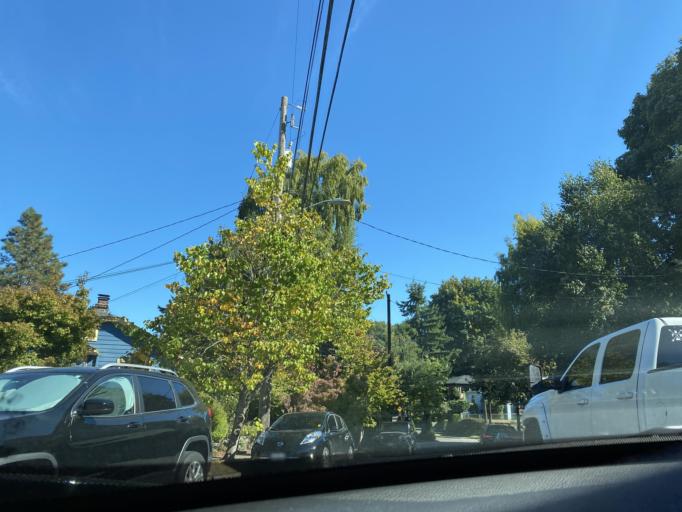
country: US
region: Washington
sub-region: King County
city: Seattle
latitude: 47.6447
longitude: -122.3525
